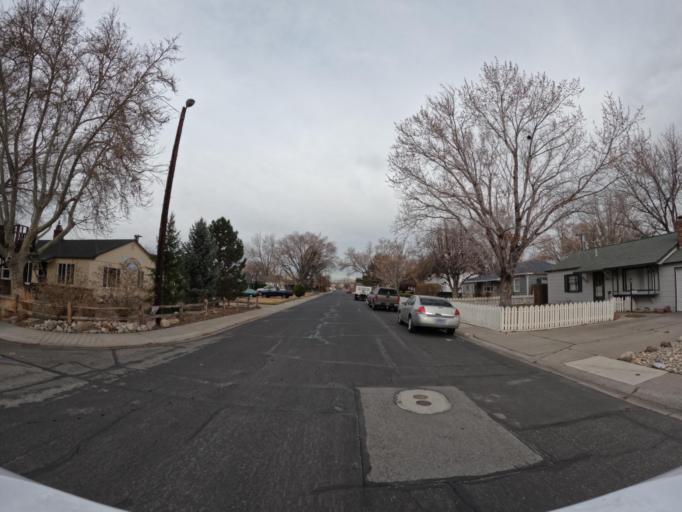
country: US
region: Nevada
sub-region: Washoe County
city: Sparks
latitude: 39.5430
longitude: -119.7496
